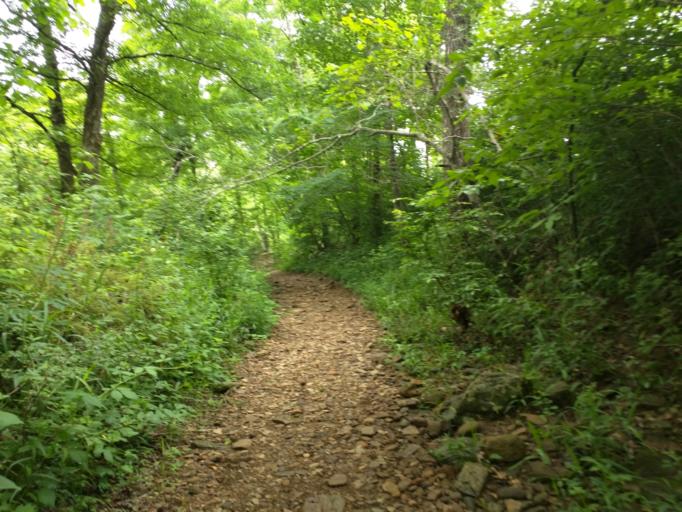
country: US
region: Arkansas
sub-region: Madison County
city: Huntsville
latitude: 35.8976
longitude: -93.5795
